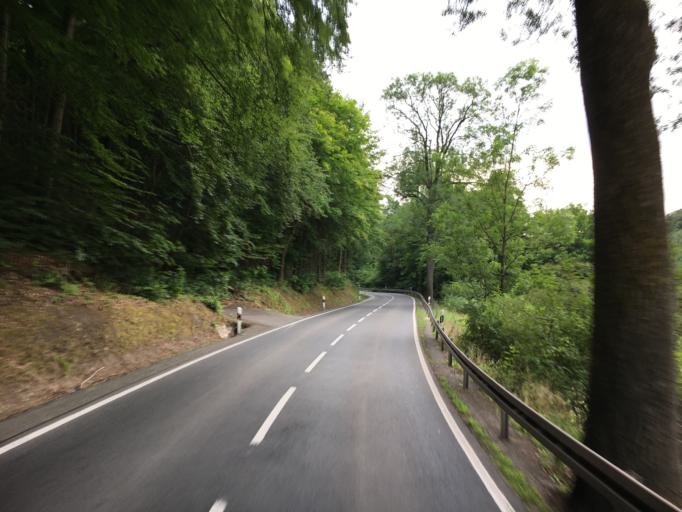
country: DE
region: Thuringia
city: Trusetal
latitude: 50.8005
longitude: 10.4305
